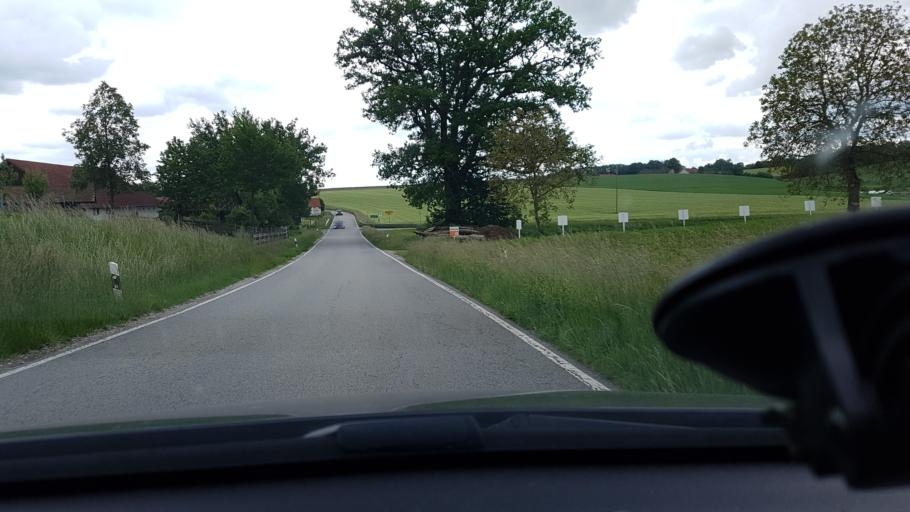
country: DE
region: Bavaria
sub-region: Lower Bavaria
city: Rotthalmunster
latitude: 48.3441
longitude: 13.1975
